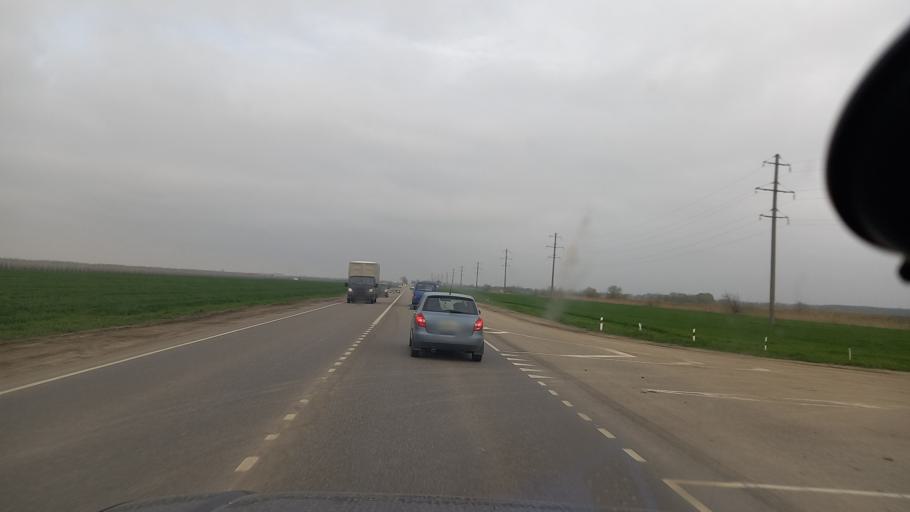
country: RU
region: Krasnodarskiy
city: Slavyansk-na-Kubani
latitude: 45.2402
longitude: 38.0206
